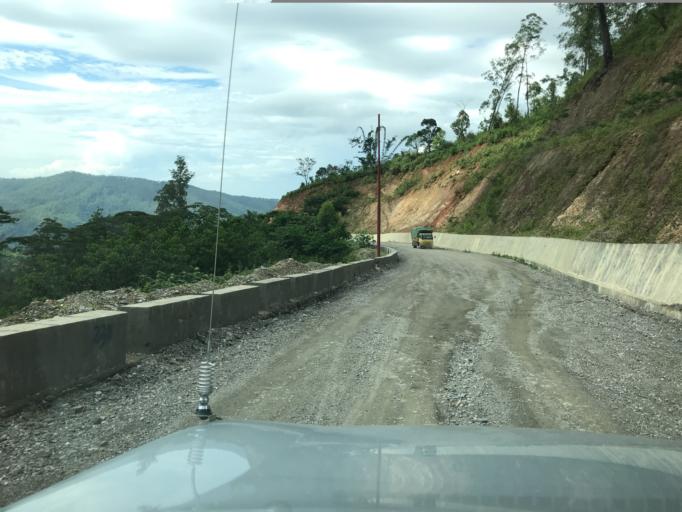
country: TL
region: Aileu
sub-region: Aileu Villa
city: Aileu
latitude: -8.6589
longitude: 125.5286
